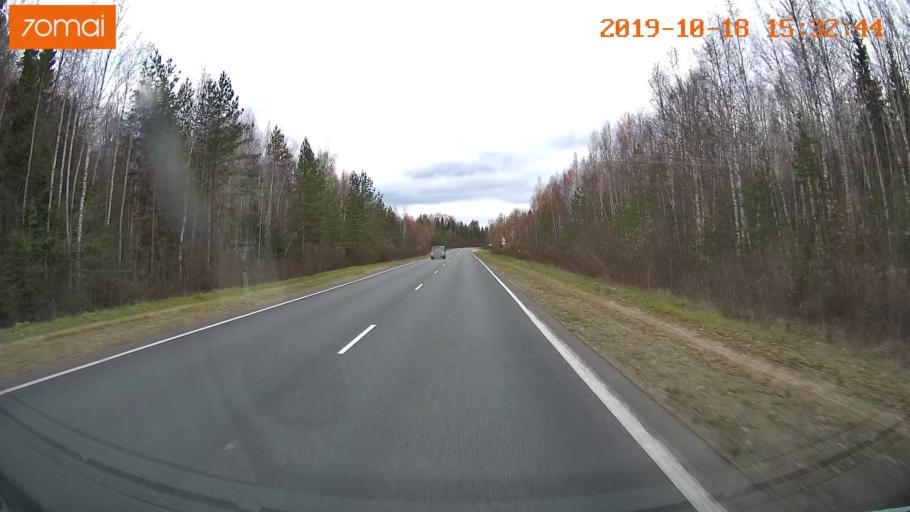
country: RU
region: Vladimir
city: Anopino
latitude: 55.8302
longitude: 40.6483
